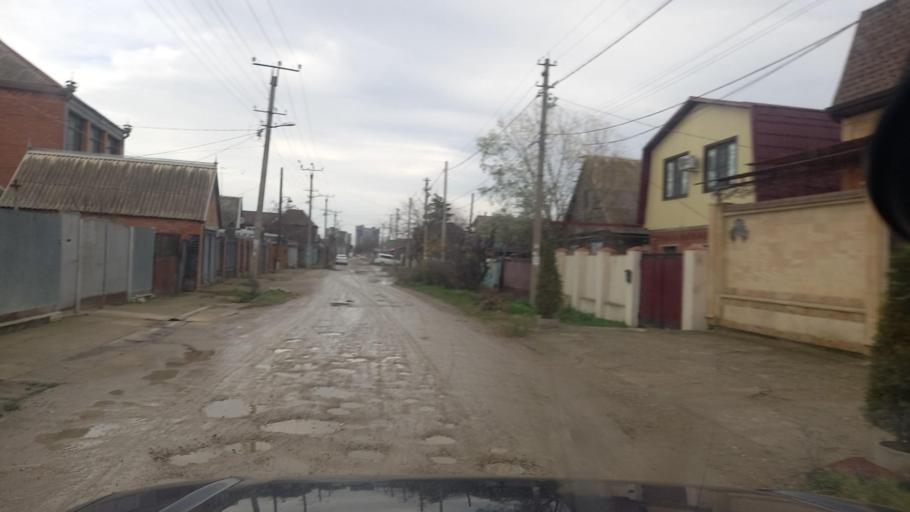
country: RU
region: Adygeya
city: Yablonovskiy
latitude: 44.9853
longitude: 38.9472
